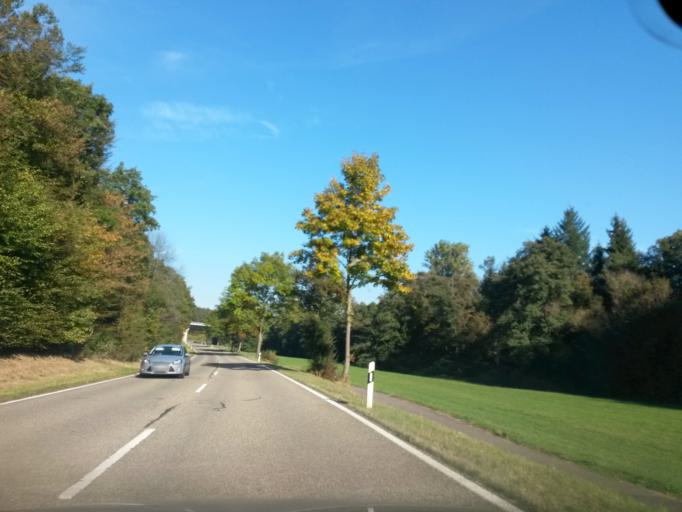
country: DE
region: Baden-Wuerttemberg
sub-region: Karlsruhe Region
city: Konigsbach-Stein
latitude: 48.9353
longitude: 8.5159
